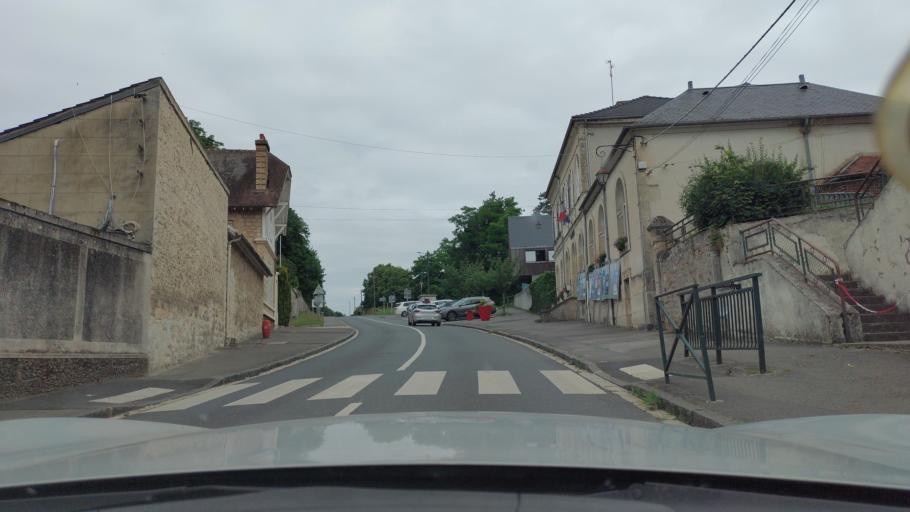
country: FR
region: Picardie
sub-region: Departement de l'Oise
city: Betz
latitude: 49.1571
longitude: 2.9537
